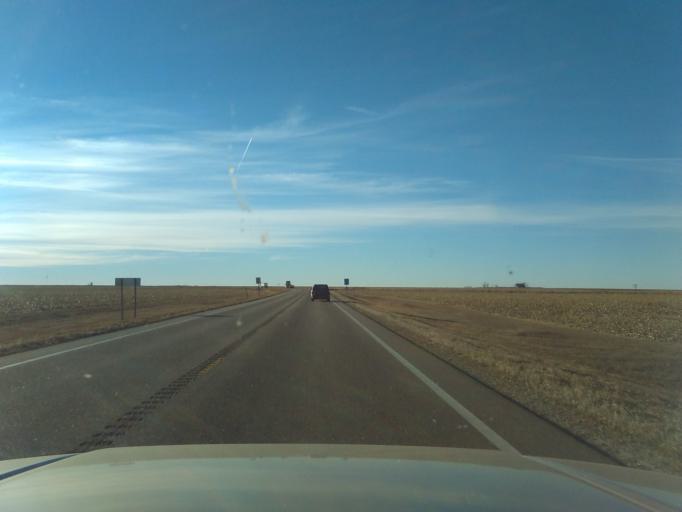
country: US
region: Kansas
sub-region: Thomas County
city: Colby
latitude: 39.4649
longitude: -100.7583
